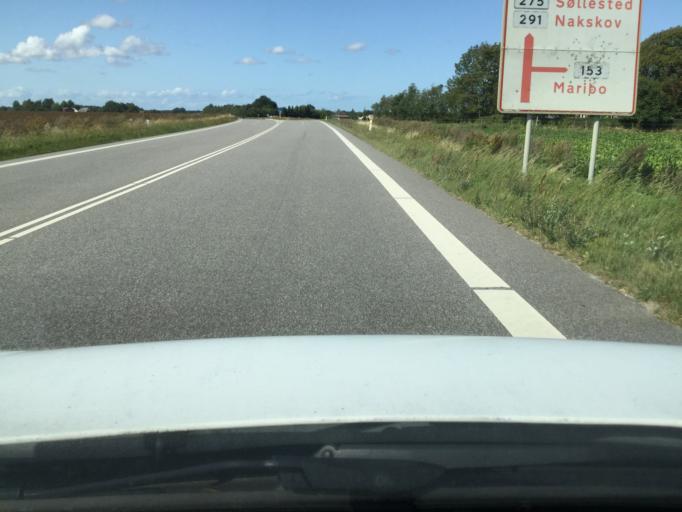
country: DK
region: Zealand
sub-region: Lolland Kommune
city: Rodby
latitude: 54.7446
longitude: 11.3878
